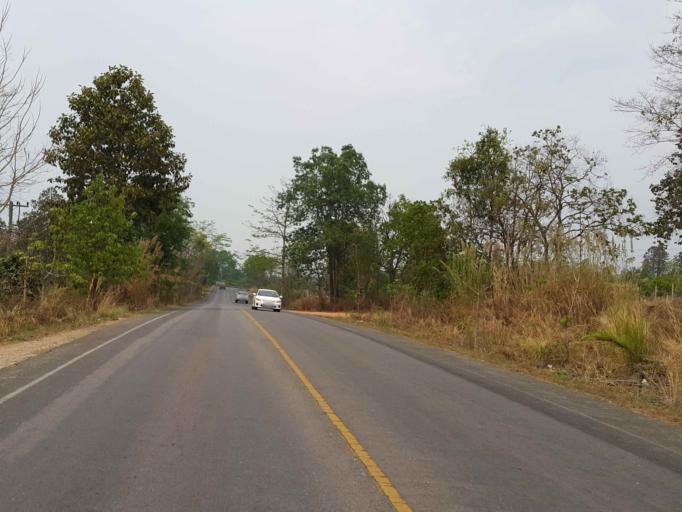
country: TH
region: Chiang Mai
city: Mae Taeng
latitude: 19.1107
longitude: 99.0005
